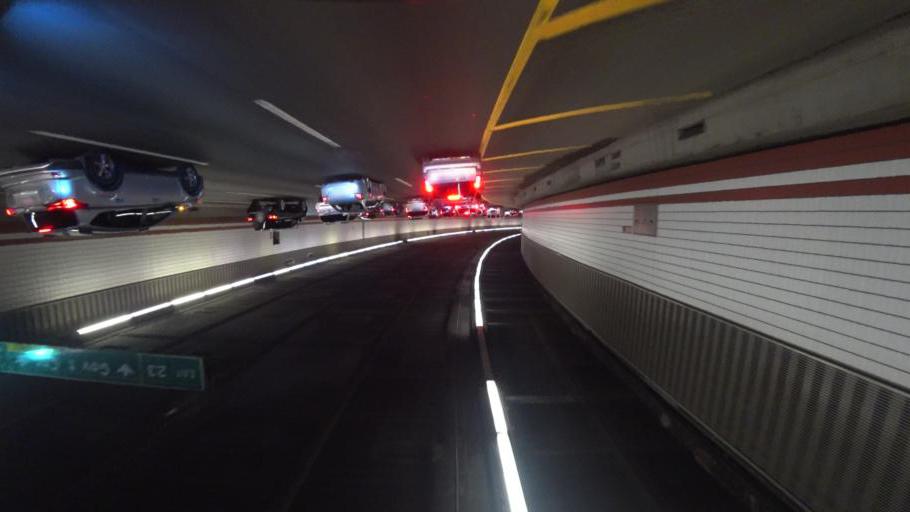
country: US
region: Massachusetts
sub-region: Suffolk County
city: Boston
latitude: 42.3587
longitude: -71.0592
